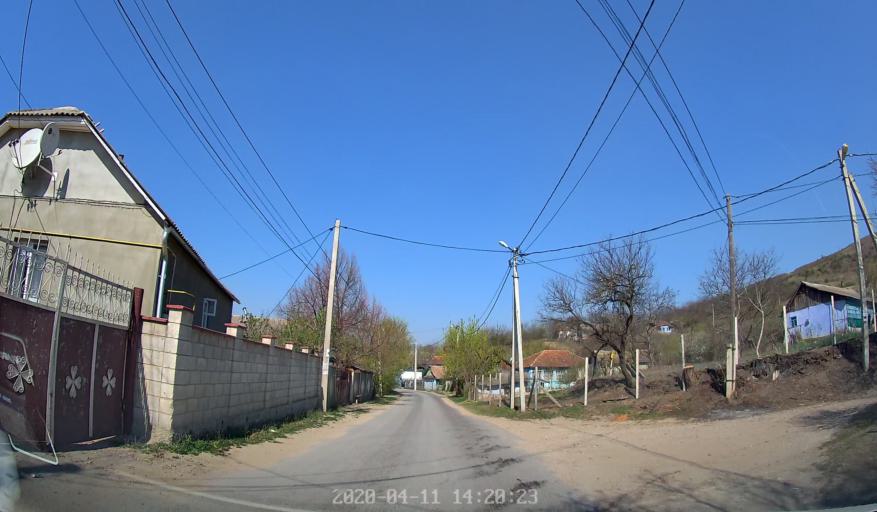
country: MD
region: Chisinau
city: Vadul lui Voda
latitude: 47.0853
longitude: 29.1337
